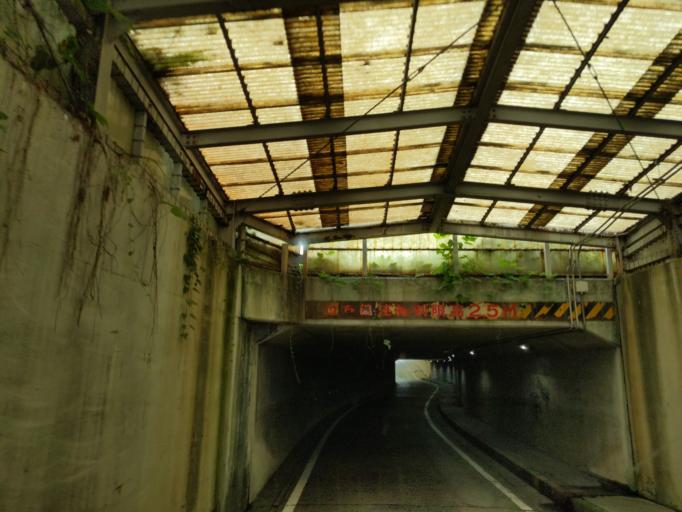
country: JP
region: Fukushima
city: Koriyama
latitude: 37.3861
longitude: 140.3812
